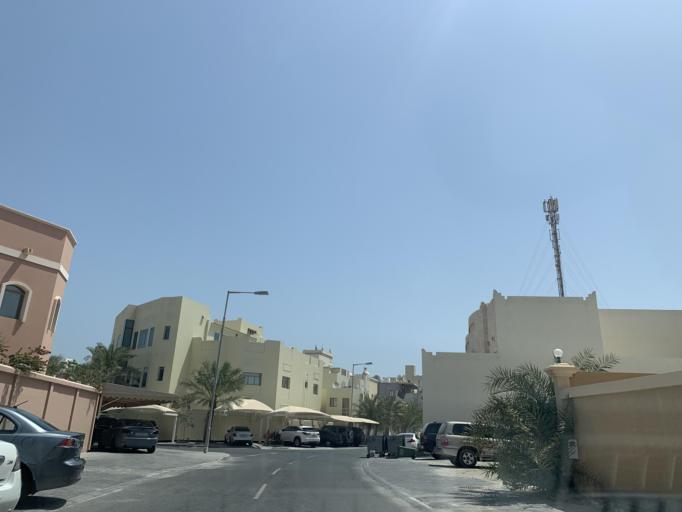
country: BH
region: Muharraq
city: Al Muharraq
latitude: 26.2772
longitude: 50.6066
